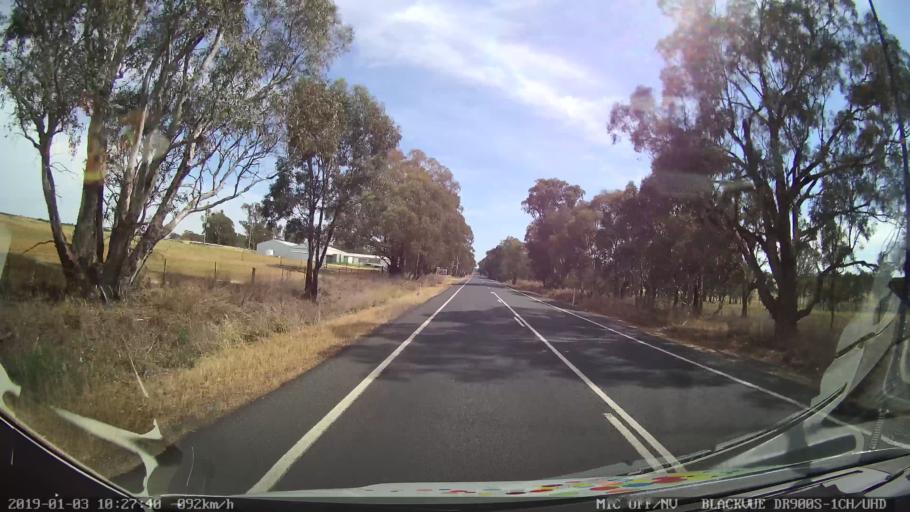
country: AU
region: New South Wales
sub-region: Young
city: Young
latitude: -34.3987
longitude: 148.2586
